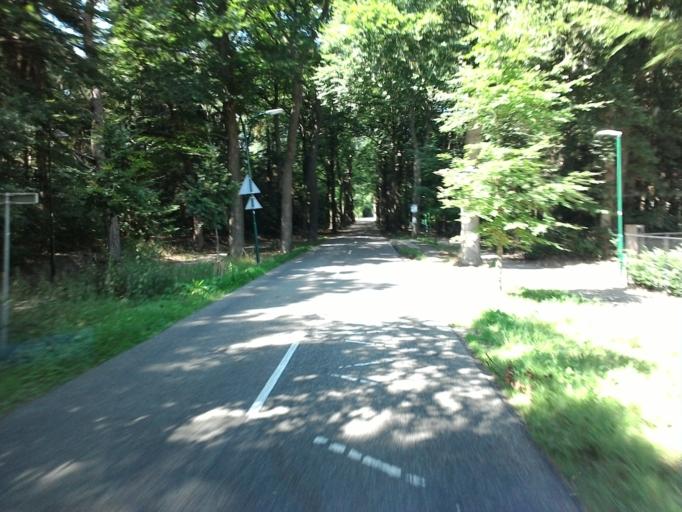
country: NL
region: Utrecht
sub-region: Gemeente De Bilt
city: De Bilt
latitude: 52.1550
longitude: 5.2036
